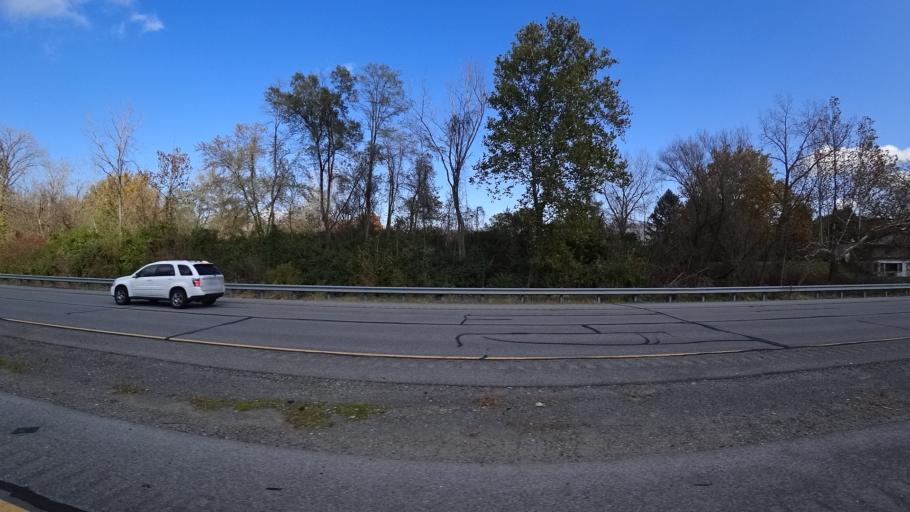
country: US
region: Indiana
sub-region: LaPorte County
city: Trail Creek
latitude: 41.7051
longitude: -86.8553
